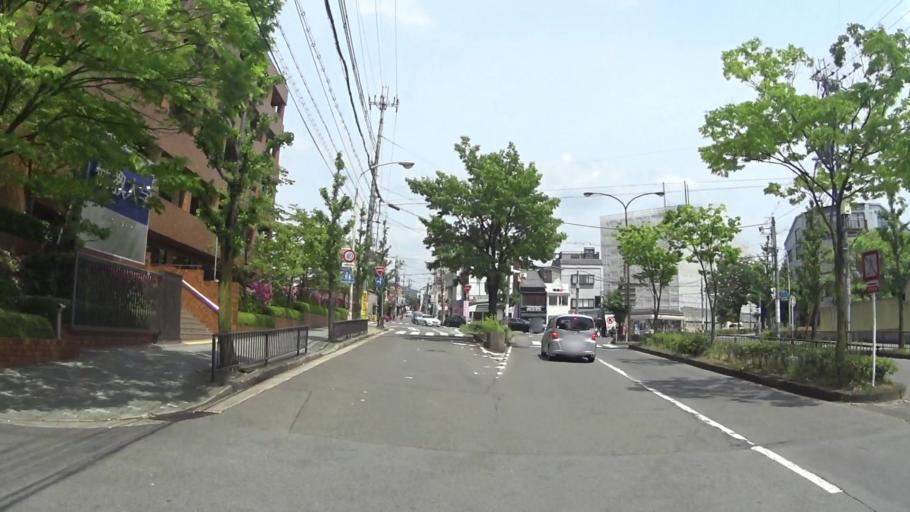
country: JP
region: Kyoto
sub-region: Kyoto-shi
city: Kamigyo-ku
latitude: 35.0443
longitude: 135.7382
